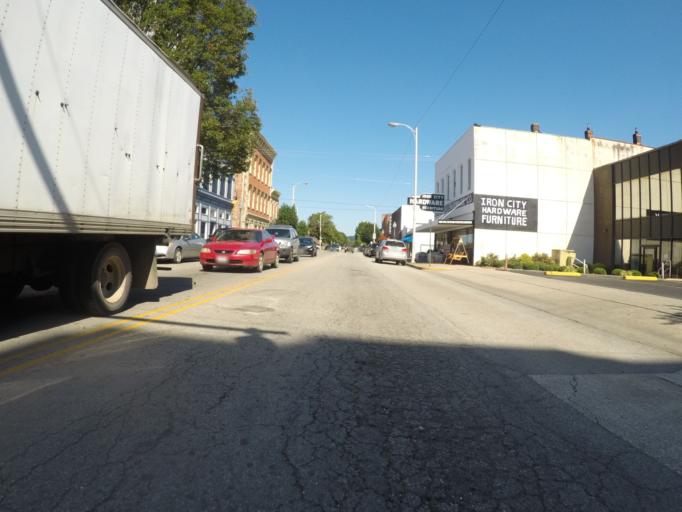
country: US
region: Ohio
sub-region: Lawrence County
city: Ironton
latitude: 38.5344
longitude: -82.6857
